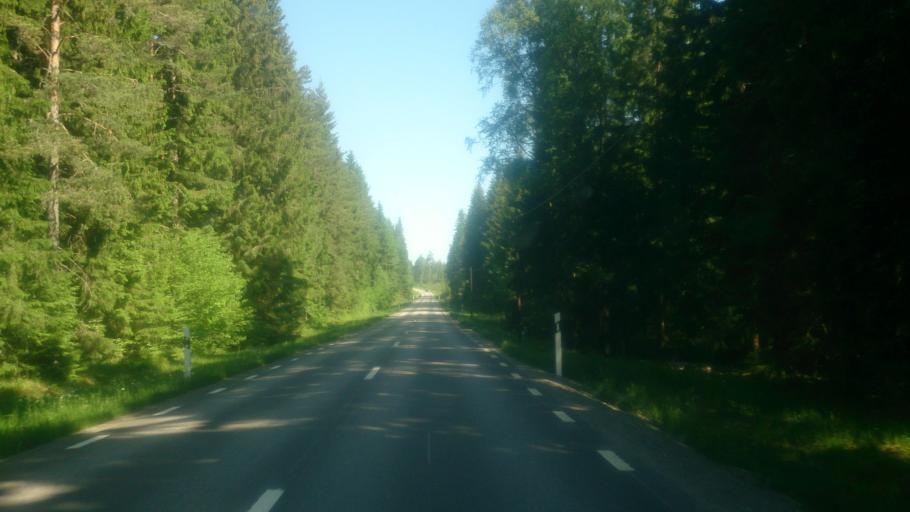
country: SE
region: OEstergoetland
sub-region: Atvidabergs Kommun
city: Atvidaberg
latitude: 58.1281
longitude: 16.0931
